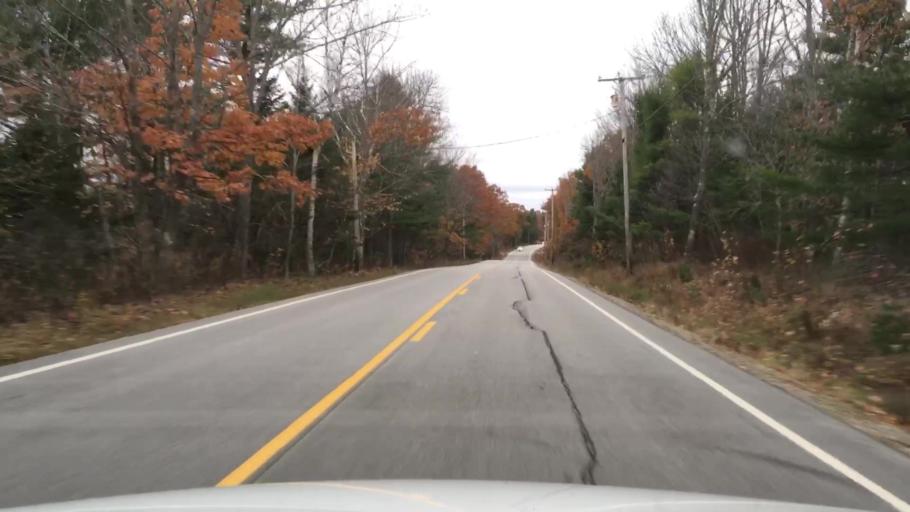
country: US
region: Maine
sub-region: Hancock County
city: Orland
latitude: 44.5396
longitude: -68.6821
